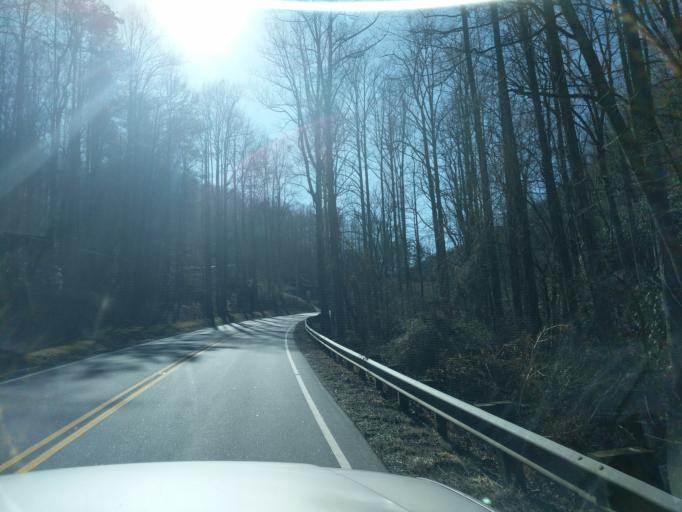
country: US
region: North Carolina
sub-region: Graham County
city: Robbinsville
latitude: 35.2657
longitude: -83.6886
